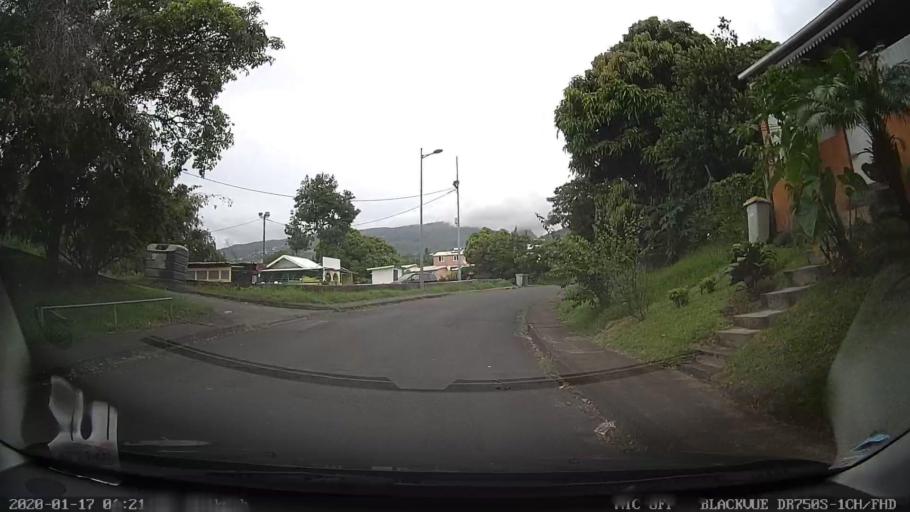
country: RE
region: Reunion
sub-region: Reunion
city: Saint-Denis
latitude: -20.9145
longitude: 55.4869
